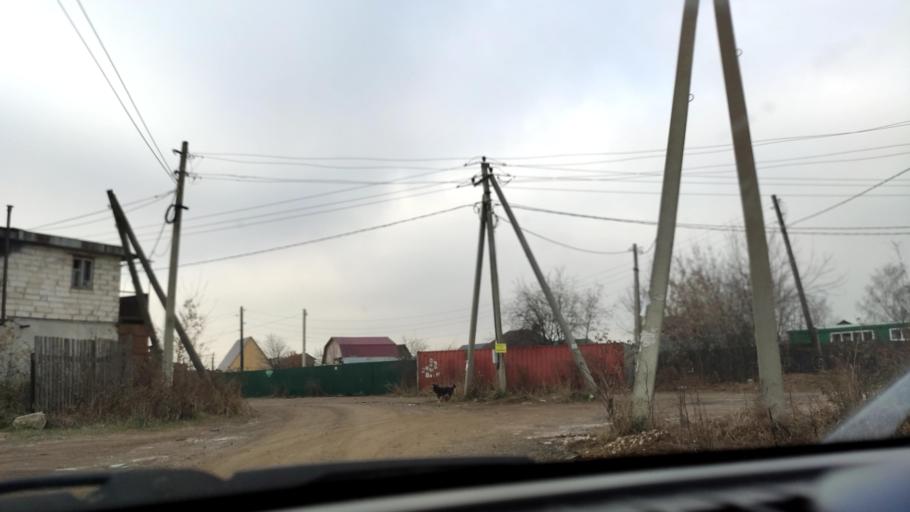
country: RU
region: Perm
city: Kondratovo
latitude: 57.9563
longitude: 56.1723
